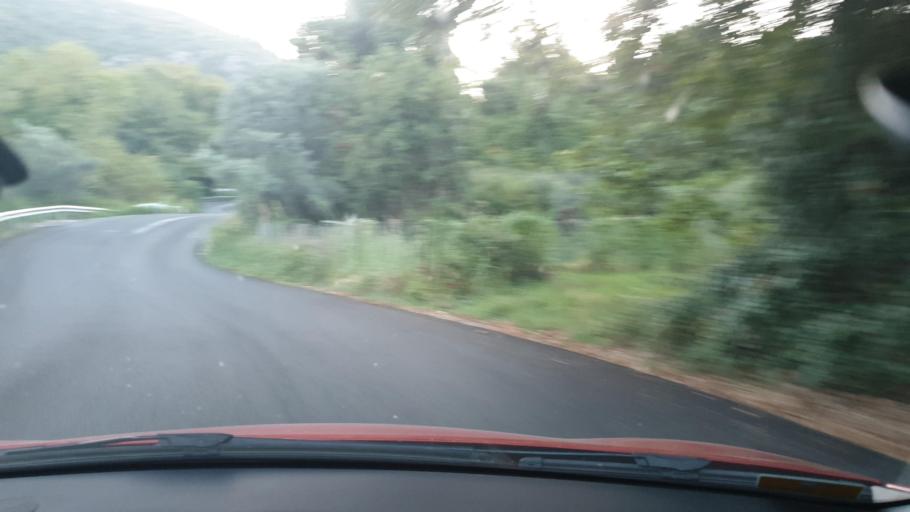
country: GR
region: Central Greece
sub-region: Nomos Evvoias
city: Kymi
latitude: 38.6312
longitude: 24.1119
